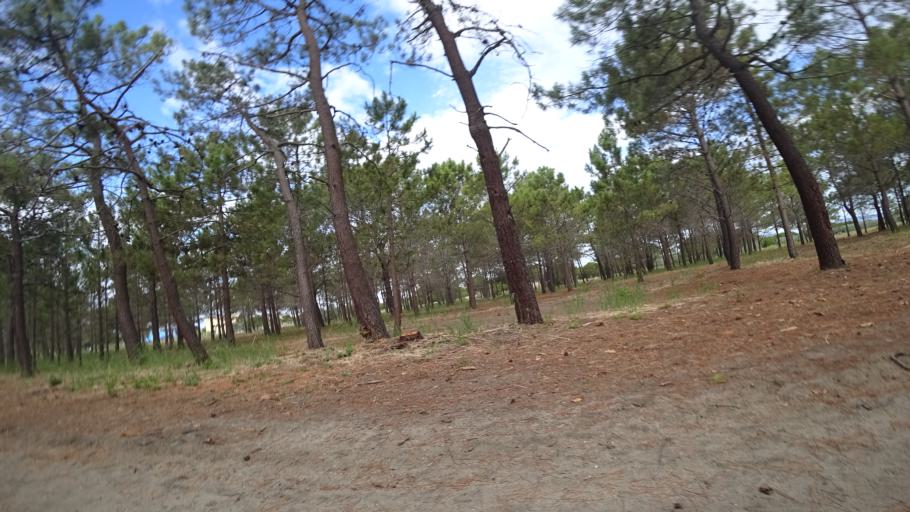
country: FR
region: Languedoc-Roussillon
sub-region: Departement des Pyrenees-Orientales
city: Le Barcares
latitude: 42.8166
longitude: 3.0334
